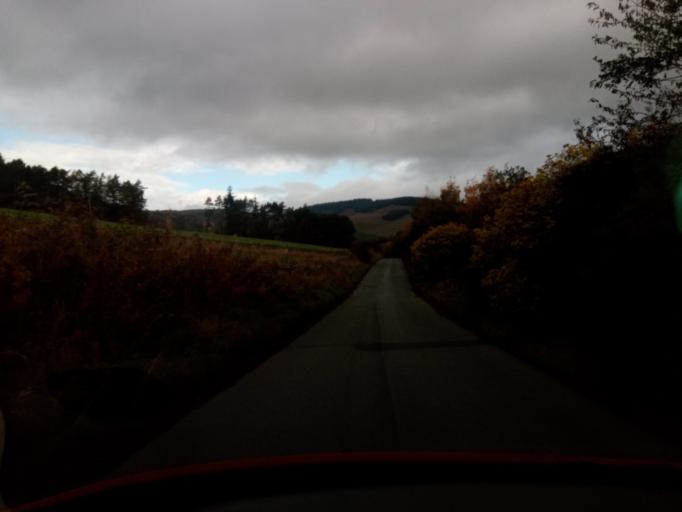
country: GB
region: Scotland
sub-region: The Scottish Borders
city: Innerleithen
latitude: 55.6363
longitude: -3.1077
